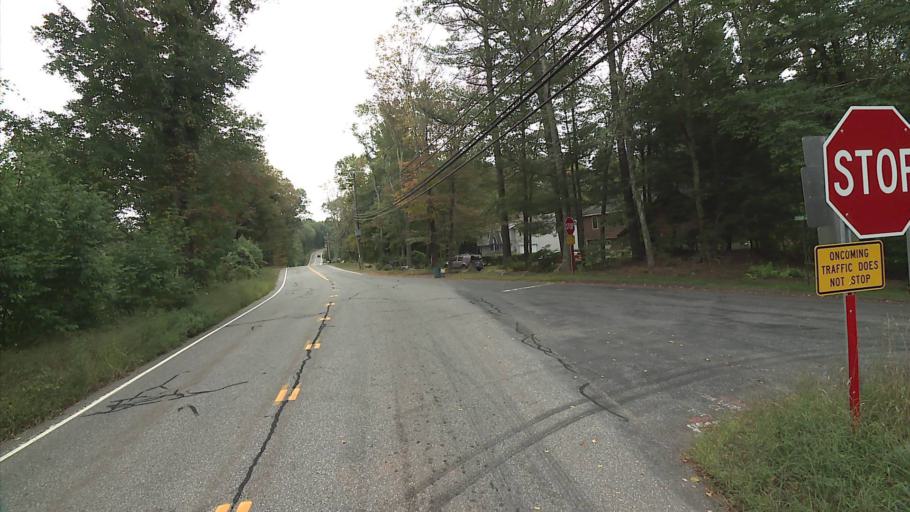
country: US
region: Connecticut
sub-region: Tolland County
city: Storrs
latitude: 41.8390
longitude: -72.2716
